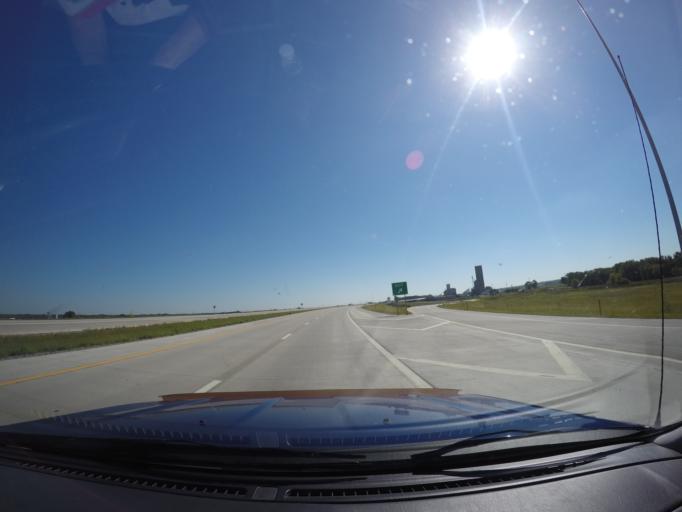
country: US
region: Kansas
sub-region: Shawnee County
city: Topeka
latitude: 39.0915
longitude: -95.7520
